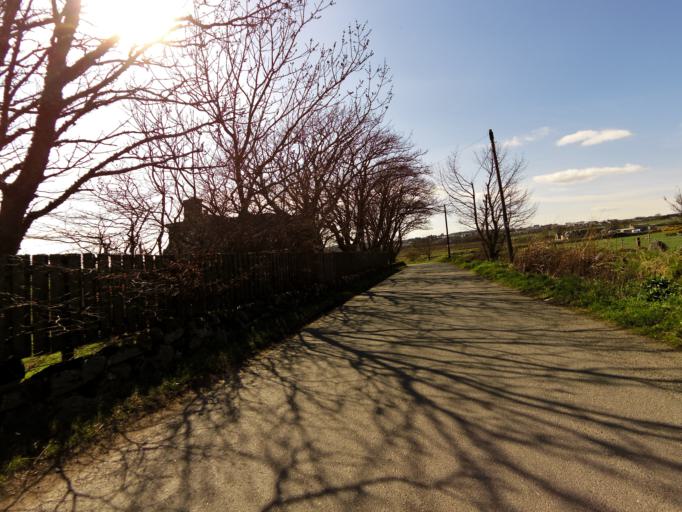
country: GB
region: Scotland
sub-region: Aberdeenshire
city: Portlethen
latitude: 57.0680
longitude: -2.1151
